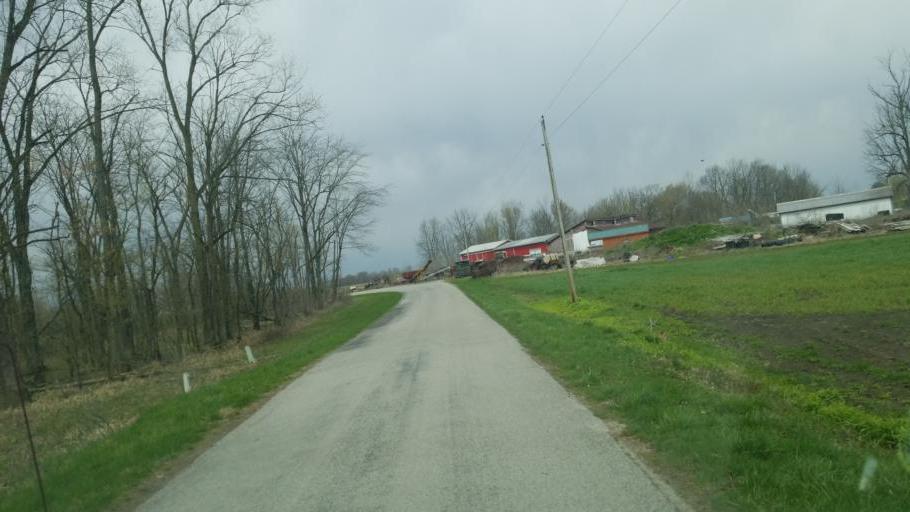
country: US
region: Ohio
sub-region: Union County
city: Richwood
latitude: 40.3914
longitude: -83.2551
